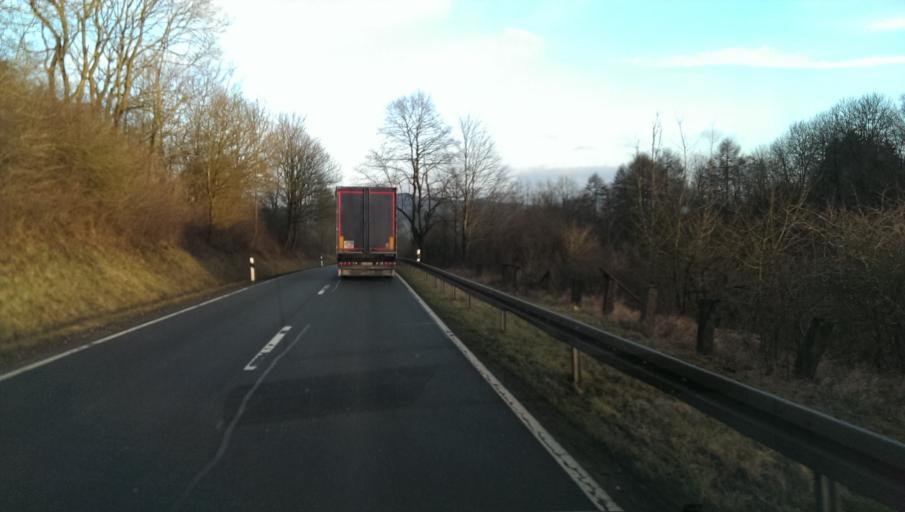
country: DE
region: Lower Saxony
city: Stadtoldendorf
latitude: 51.8784
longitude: 9.6523
